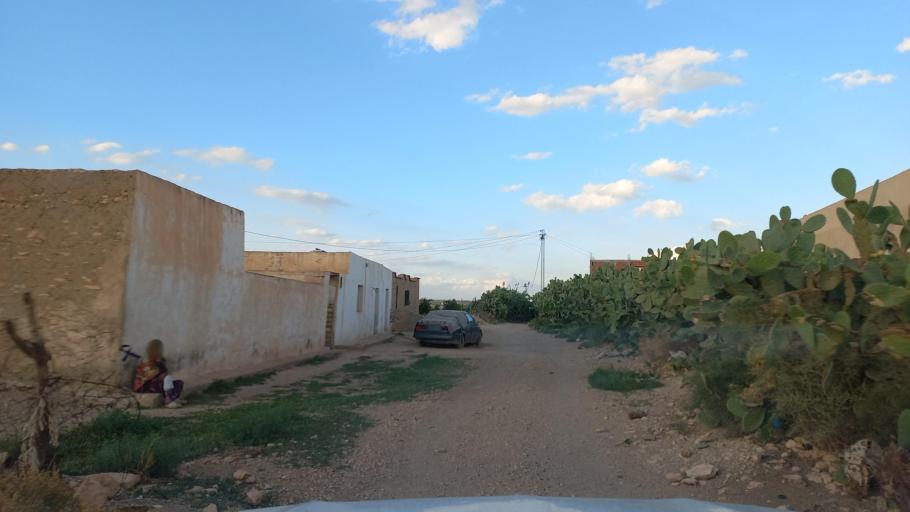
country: TN
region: Al Qasrayn
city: Sbiba
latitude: 35.3752
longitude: 9.0555
